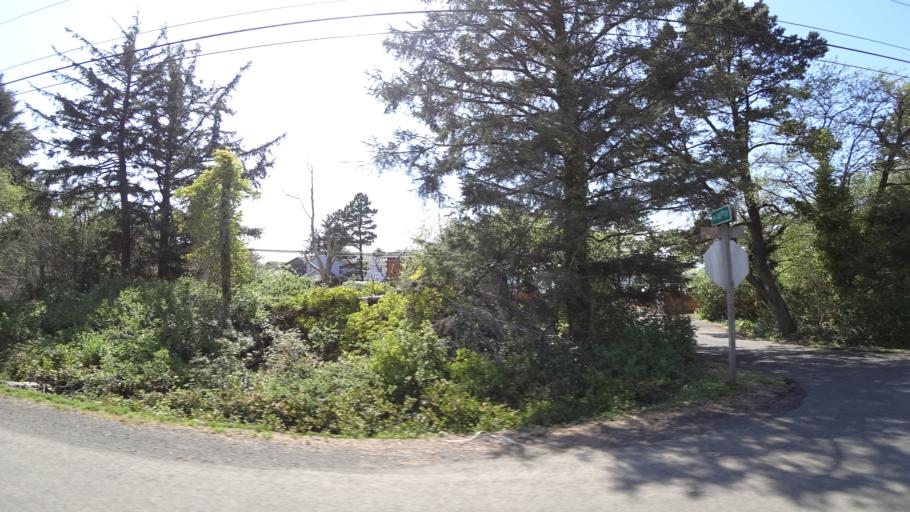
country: US
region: Oregon
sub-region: Lincoln County
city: Newport
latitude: 44.6691
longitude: -124.0578
